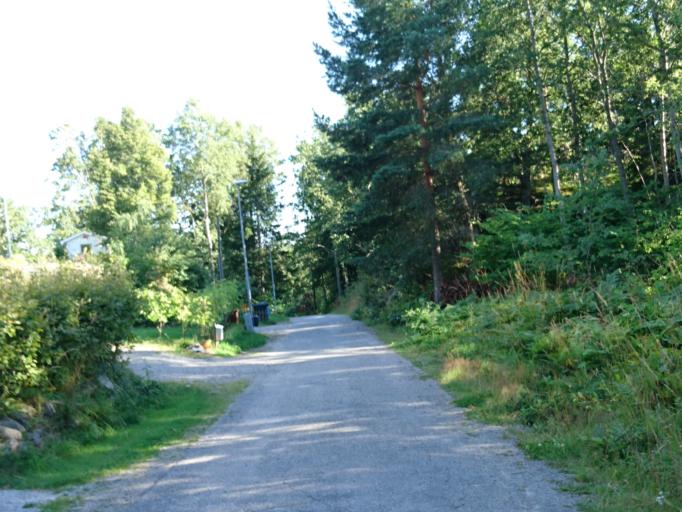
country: SE
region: Stockholm
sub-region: Huddinge Kommun
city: Segeltorp
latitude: 59.2700
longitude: 17.9460
